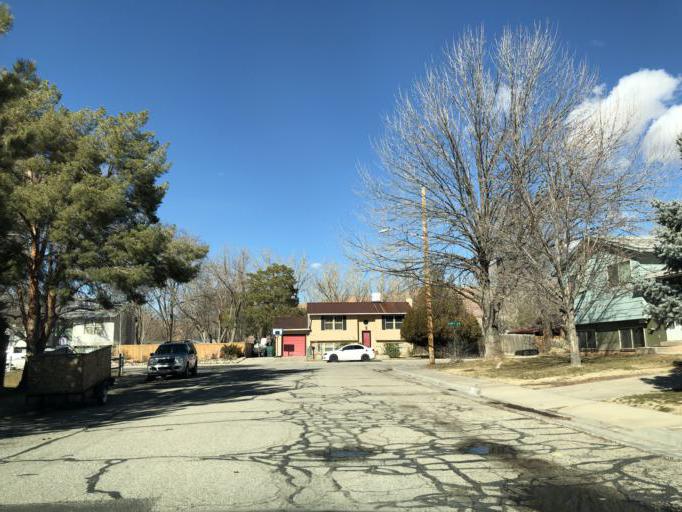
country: US
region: Utah
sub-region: Grand County
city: Moab
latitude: 38.5751
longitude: -109.5639
